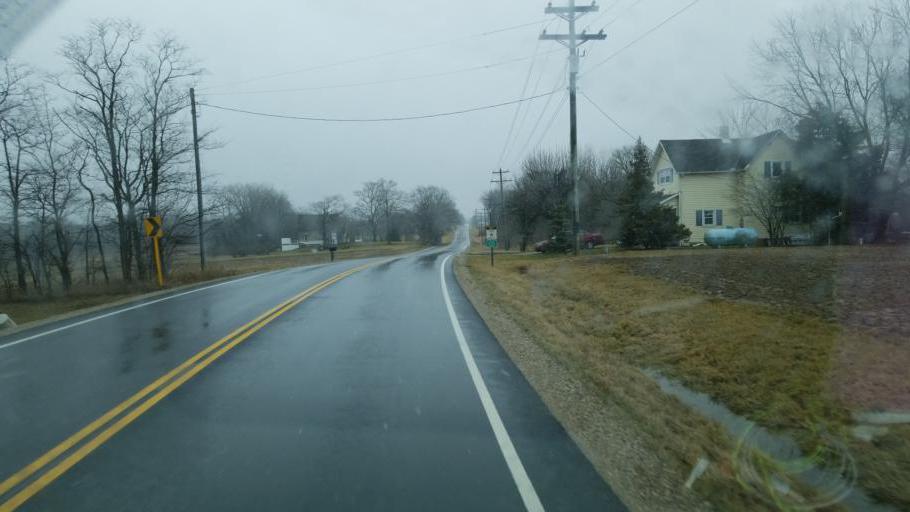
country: US
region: Ohio
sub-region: Union County
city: New California
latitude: 40.2163
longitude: -83.2866
